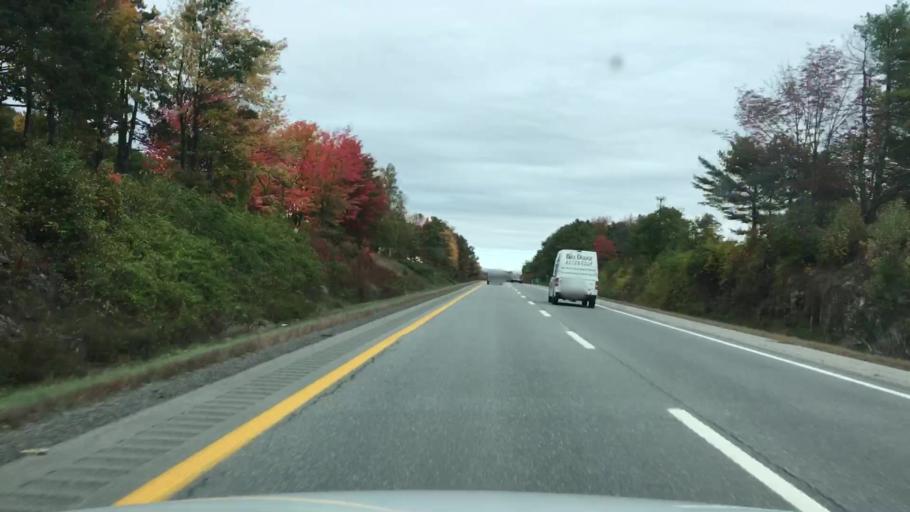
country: US
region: Maine
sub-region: Kennebec County
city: Waterville
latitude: 44.5565
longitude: -69.6746
